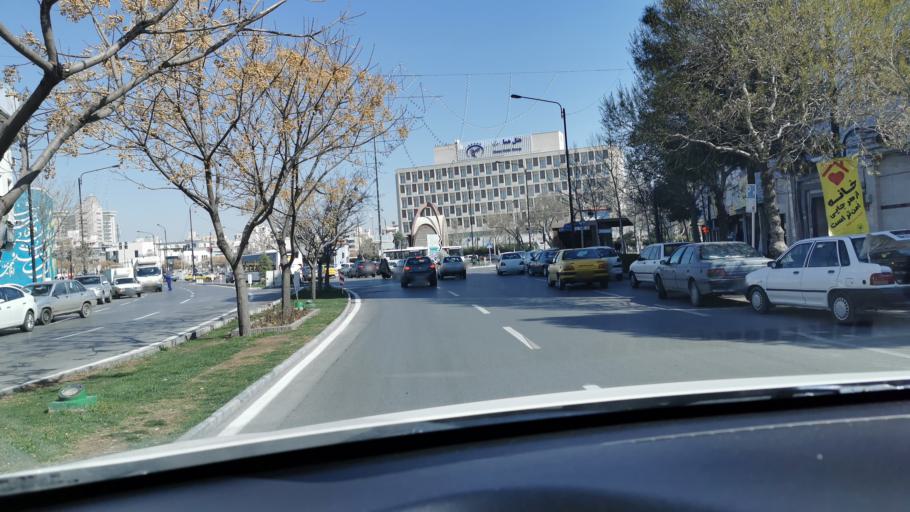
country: IR
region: Razavi Khorasan
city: Mashhad
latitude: 36.2959
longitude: 59.5731
